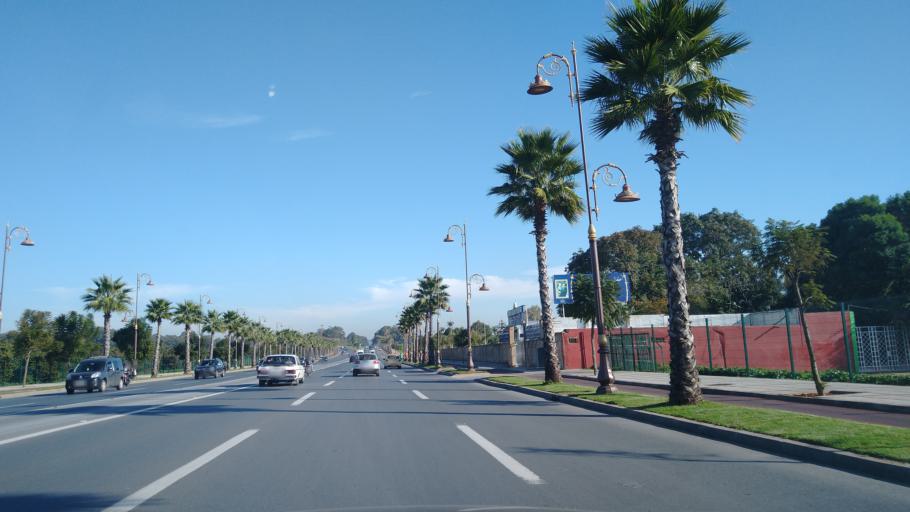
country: MA
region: Rabat-Sale-Zemmour-Zaer
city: Sale
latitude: 34.0316
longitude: -6.7616
